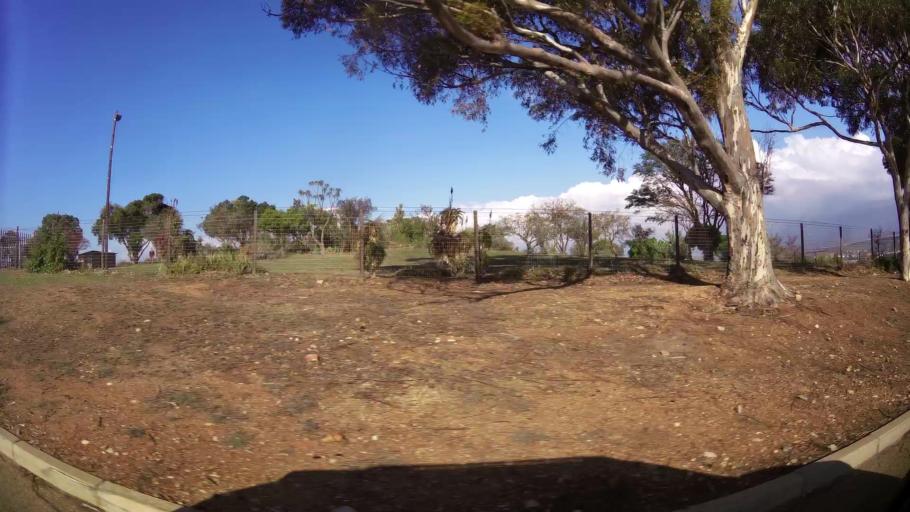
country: ZA
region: Eastern Cape
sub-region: Nelson Mandela Bay Metropolitan Municipality
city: Uitenhage
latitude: -33.7667
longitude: 25.4053
